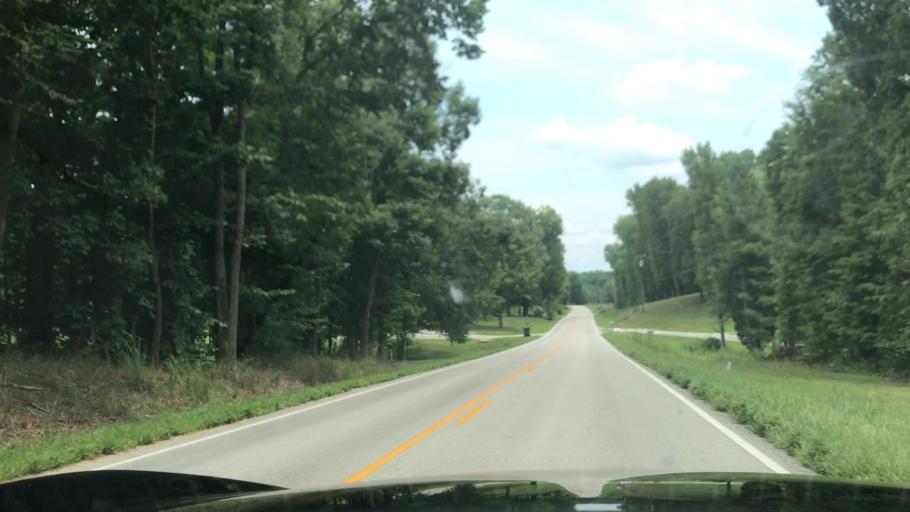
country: US
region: Kentucky
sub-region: Butler County
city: Morgantown
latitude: 37.1724
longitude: -86.8290
